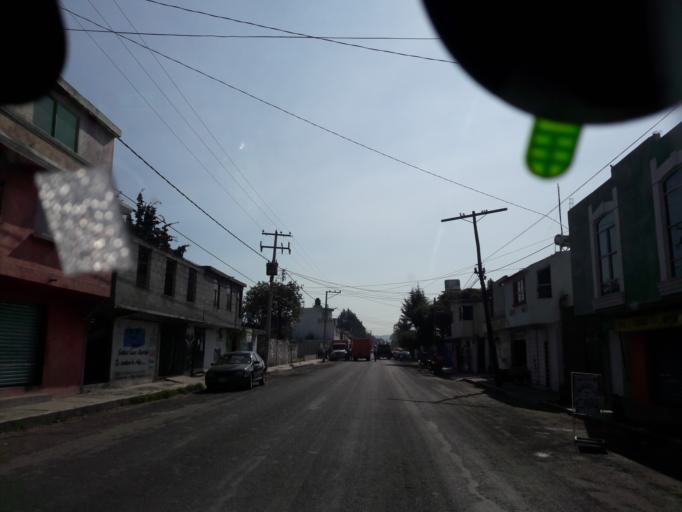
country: MX
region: Tlaxcala
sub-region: Panotla
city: Fraccionamiento la Virgen
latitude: 19.3188
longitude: -98.3118
